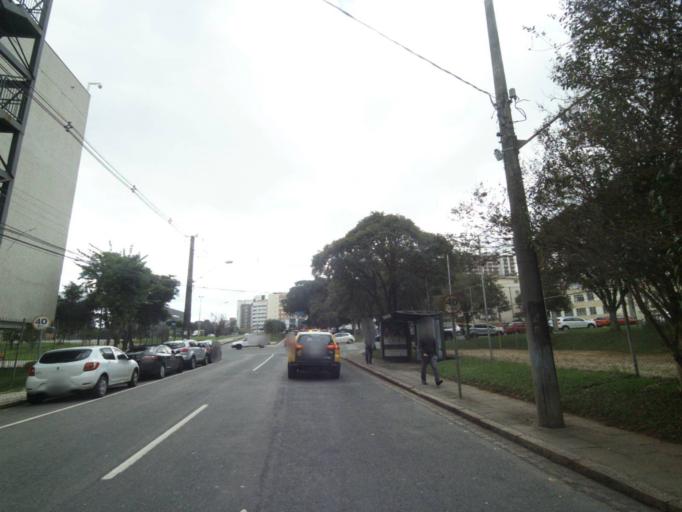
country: BR
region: Parana
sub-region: Curitiba
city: Curitiba
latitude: -25.4144
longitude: -49.2660
